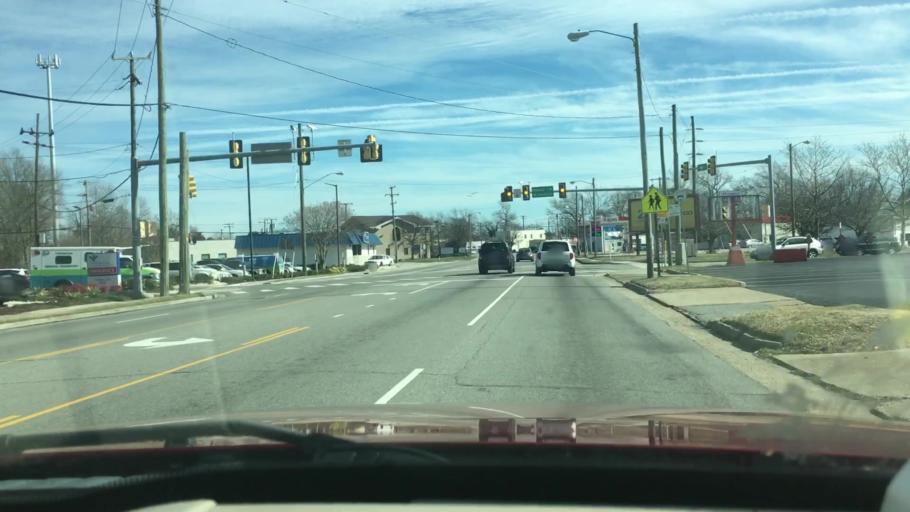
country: US
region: Virginia
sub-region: City of Portsmouth
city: Portsmouth Heights
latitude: 36.8358
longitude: -76.3477
